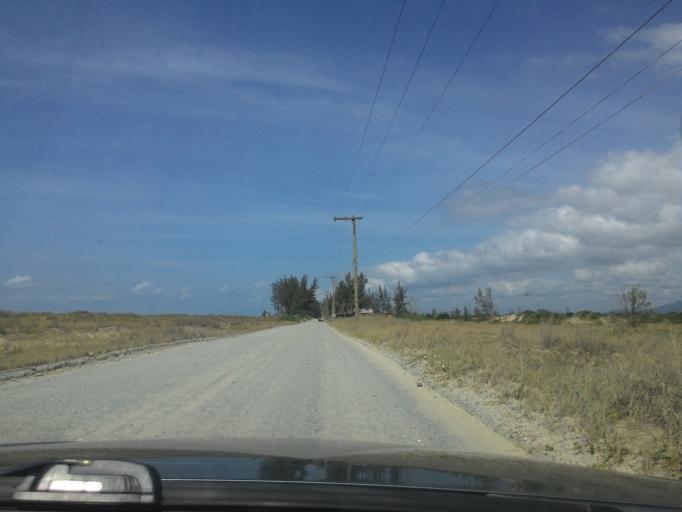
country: BR
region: Sao Paulo
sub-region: Iguape
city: Iguape
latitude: -24.8374
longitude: -47.6776
